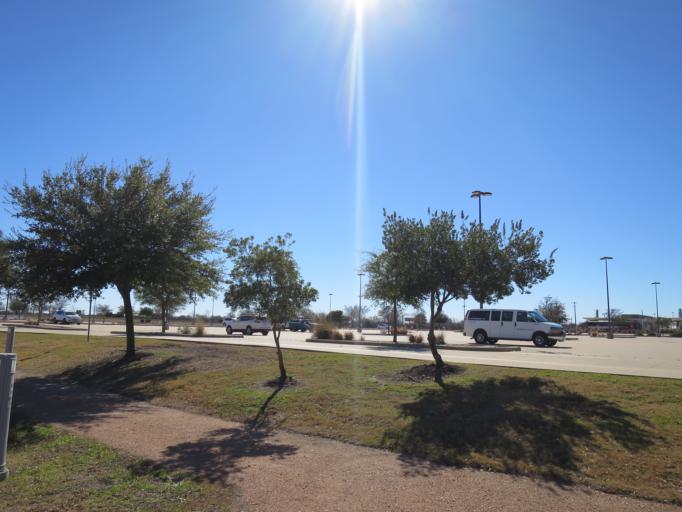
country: US
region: Texas
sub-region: Williamson County
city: Leander
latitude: 30.5876
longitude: -97.8544
